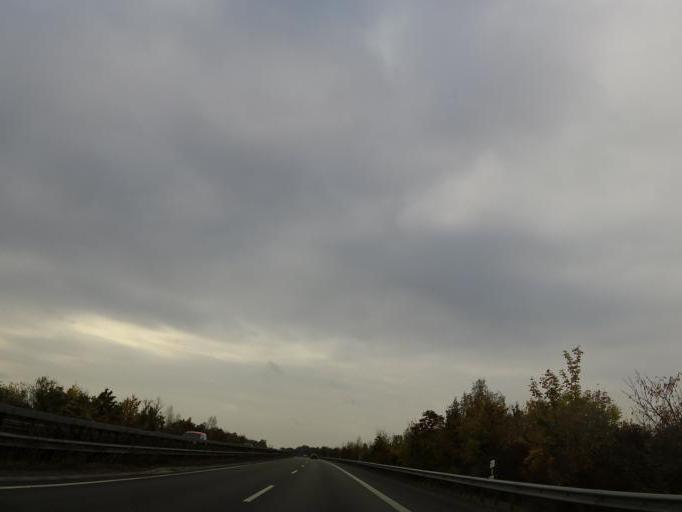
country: DE
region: Rheinland-Pfalz
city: Lonsheim
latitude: 49.7588
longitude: 8.0892
